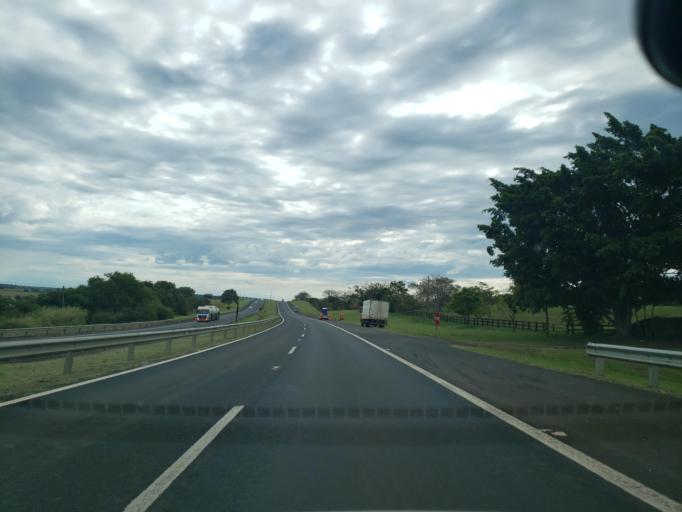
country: BR
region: Sao Paulo
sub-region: Bauru
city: Bauru
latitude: -22.2177
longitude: -49.1687
